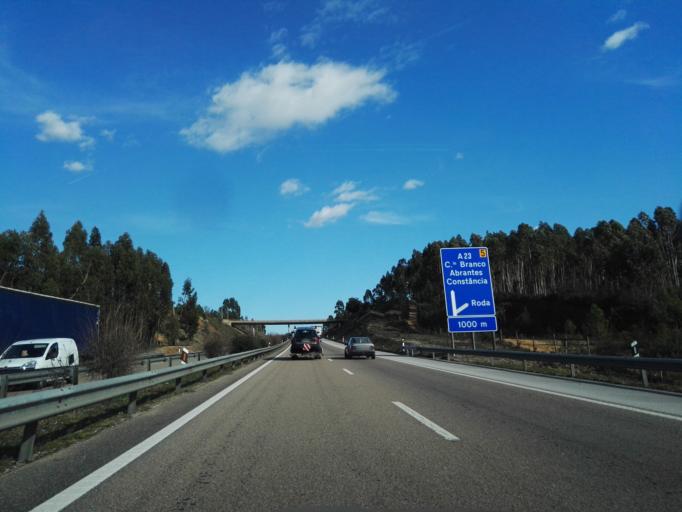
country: PT
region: Santarem
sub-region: Chamusca
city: Vila Nova da Barquinha
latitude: 39.4861
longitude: -8.4058
